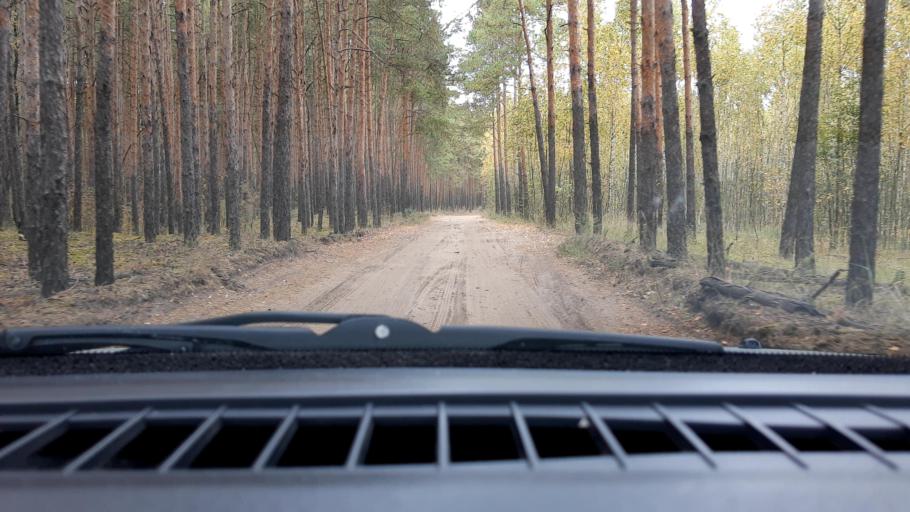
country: RU
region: Nizjnij Novgorod
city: Gorbatovka
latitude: 56.3097
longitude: 43.6991
